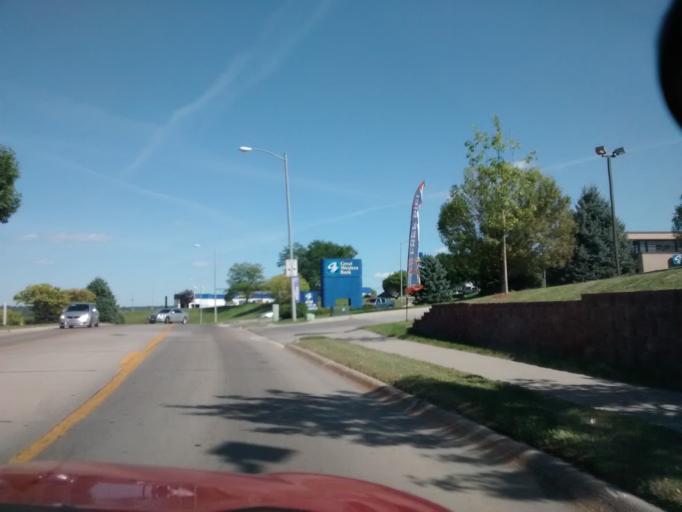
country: US
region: Nebraska
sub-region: Sarpy County
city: Offutt Air Force Base
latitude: 41.1408
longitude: -95.9698
